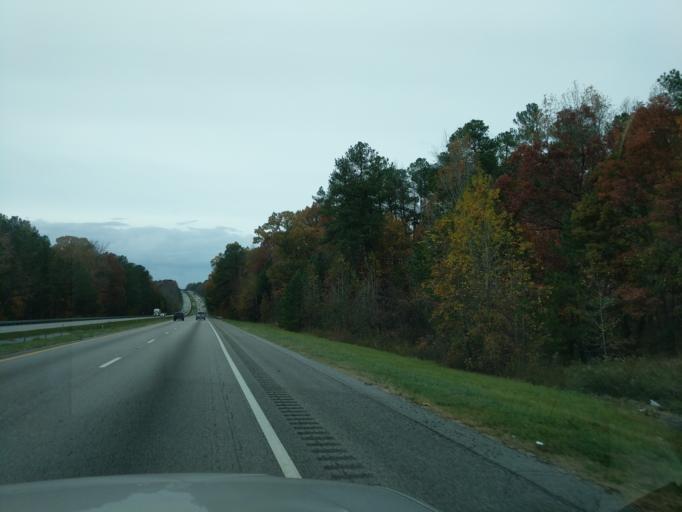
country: US
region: South Carolina
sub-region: Laurens County
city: Joanna
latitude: 34.4720
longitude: -81.8104
